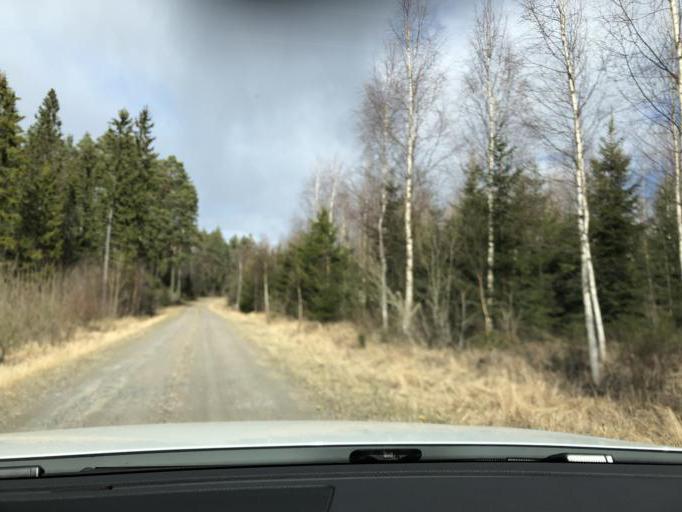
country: SE
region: Gaevleborg
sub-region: Gavle Kommun
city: Hedesunda
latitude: 60.3345
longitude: 17.1084
